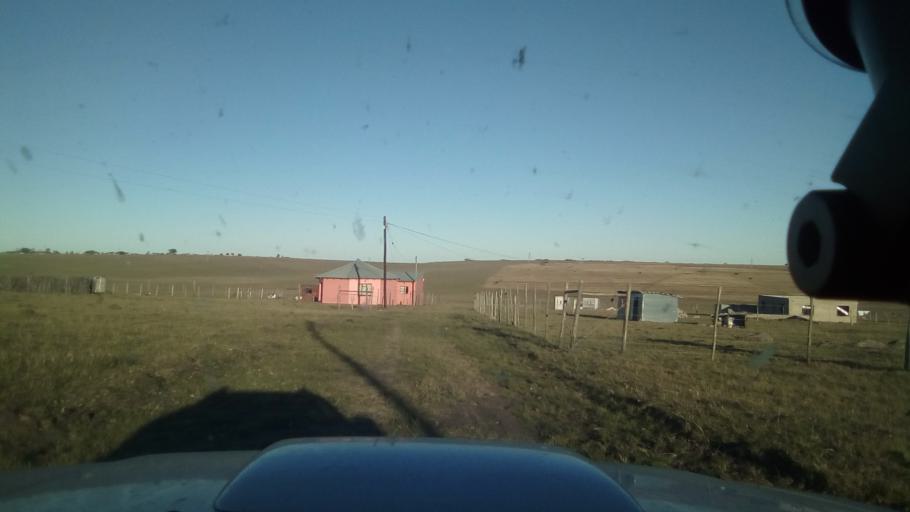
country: ZA
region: Eastern Cape
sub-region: Buffalo City Metropolitan Municipality
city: Bhisho
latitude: -32.9544
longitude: 27.3166
